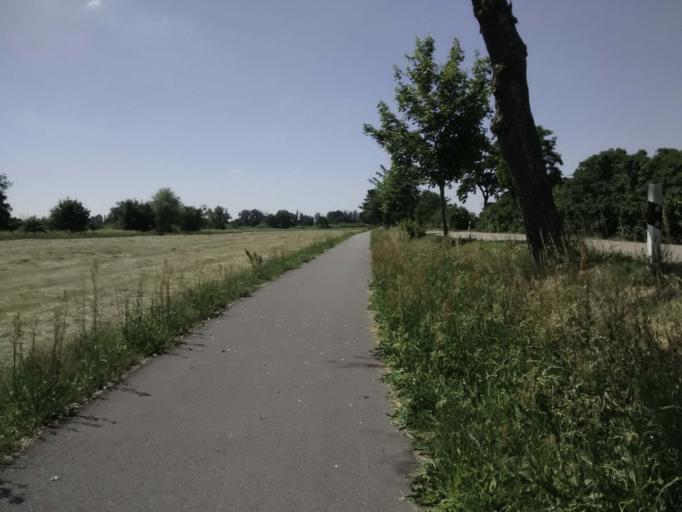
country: DE
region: Saxony-Anhalt
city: Worlitz
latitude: 51.8444
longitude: 12.4095
